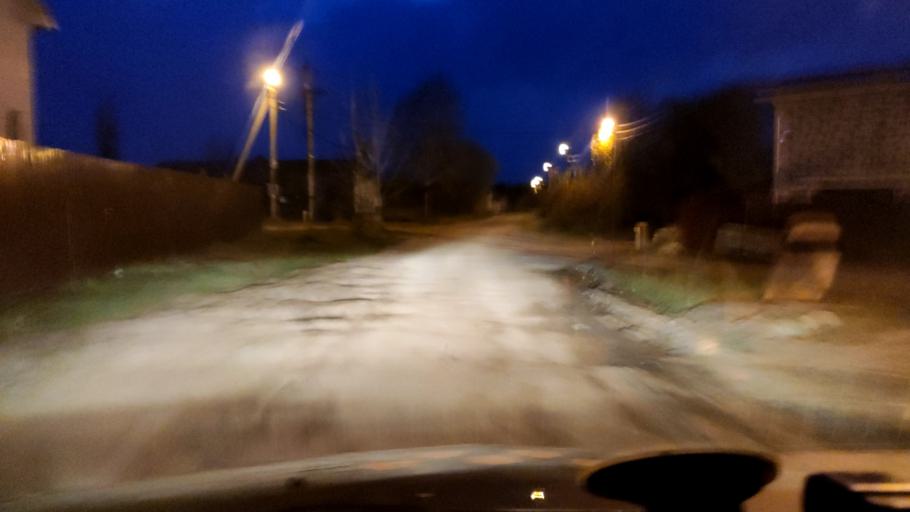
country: RU
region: Voronezj
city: Pridonskoy
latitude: 51.6322
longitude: 39.0905
